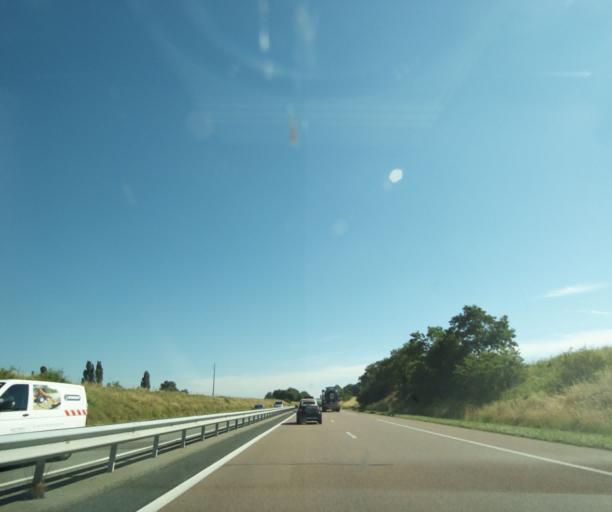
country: FR
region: Champagne-Ardenne
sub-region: Departement de la Haute-Marne
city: Saulxures
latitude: 48.0663
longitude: 5.5906
